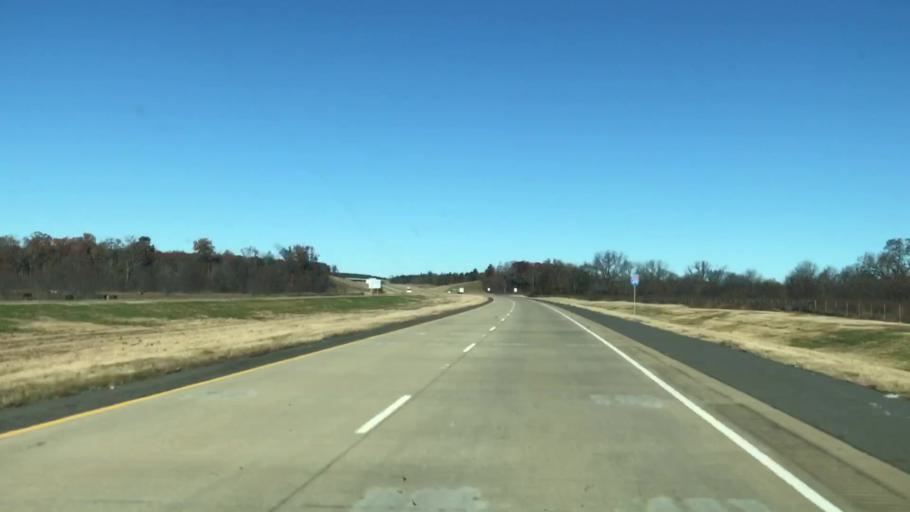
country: US
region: Louisiana
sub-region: Caddo Parish
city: Vivian
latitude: 32.9066
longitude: -93.8666
